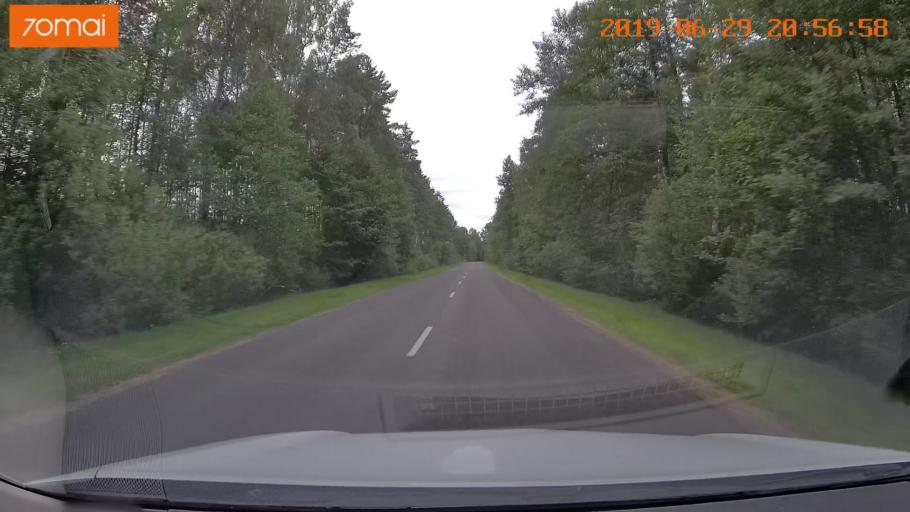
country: BY
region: Brest
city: Hantsavichy
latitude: 52.7124
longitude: 26.3690
